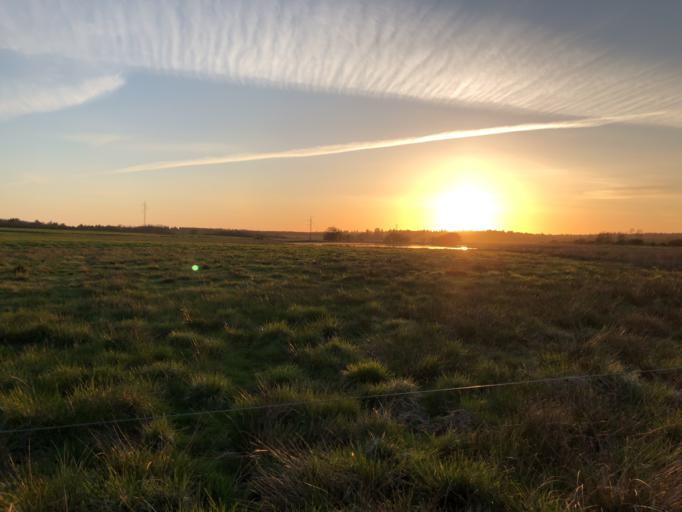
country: DK
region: Central Jutland
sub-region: Holstebro Kommune
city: Ulfborg
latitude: 56.2473
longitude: 8.4106
